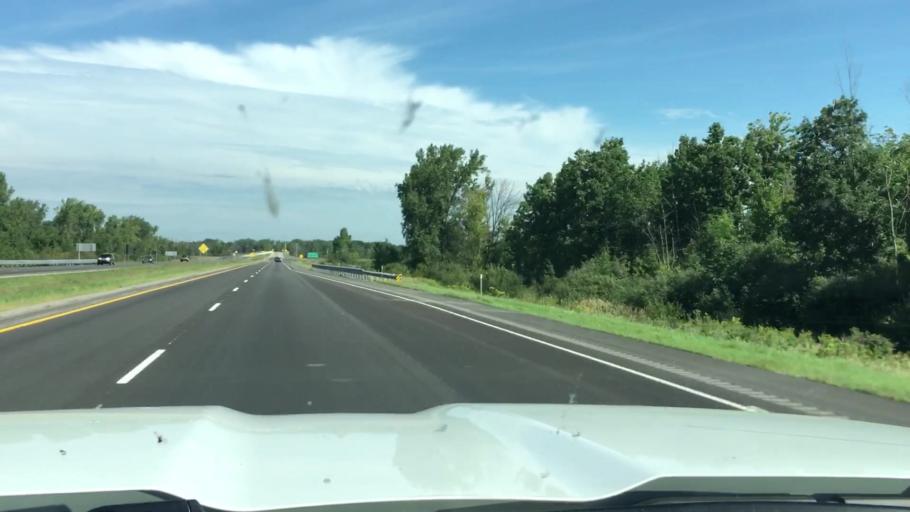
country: US
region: Michigan
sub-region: Saginaw County
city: Freeland
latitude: 43.5891
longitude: -84.1393
